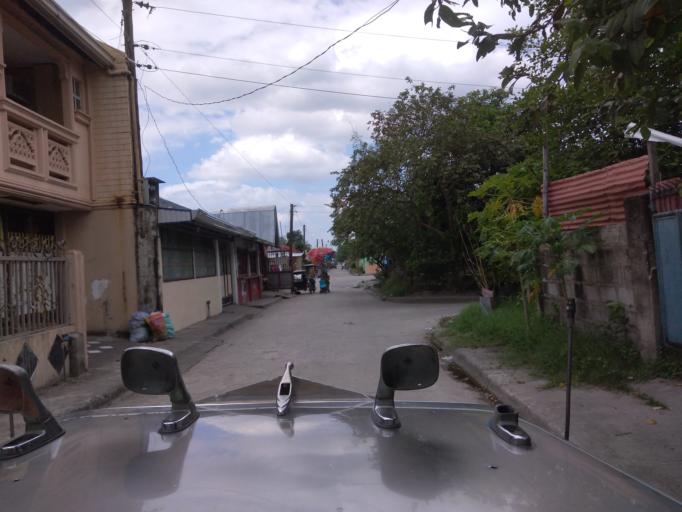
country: PH
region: Central Luzon
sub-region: Province of Pampanga
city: Pandacaqui
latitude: 15.1762
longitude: 120.6609
